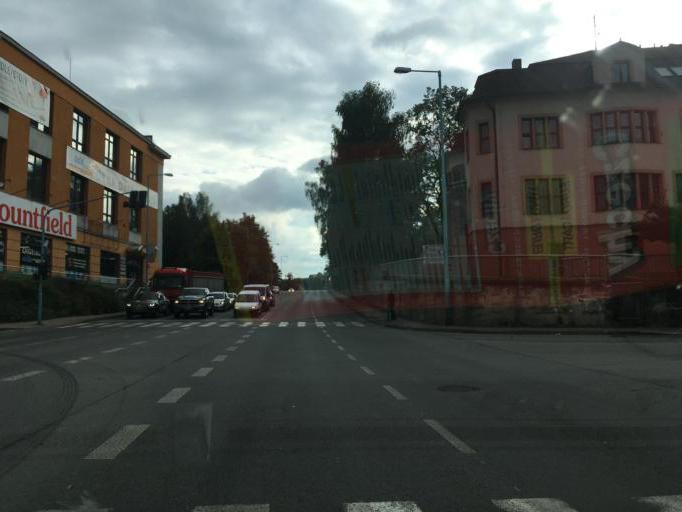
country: CZ
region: Vysocina
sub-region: Okres Pelhrimov
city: Pelhrimov
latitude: 49.4277
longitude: 15.2265
